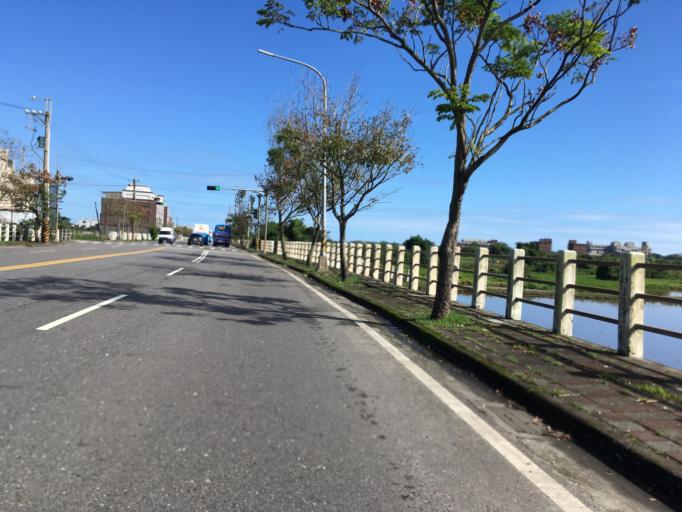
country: TW
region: Taiwan
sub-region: Yilan
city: Yilan
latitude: 24.6126
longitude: 121.8419
